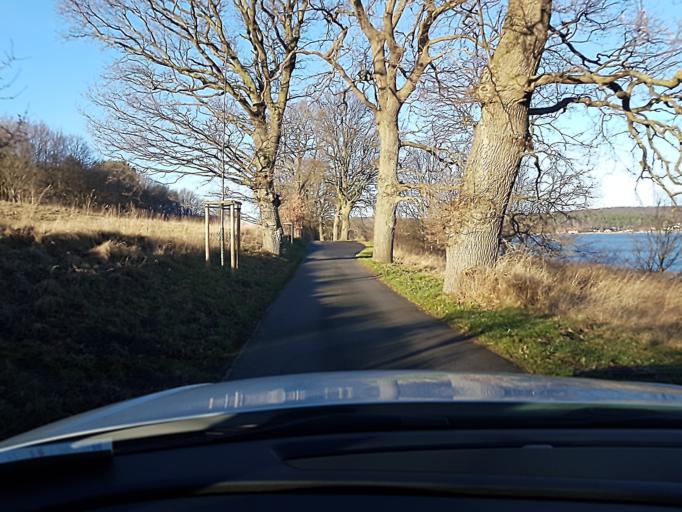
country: DE
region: Mecklenburg-Vorpommern
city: Ostseebad Sellin
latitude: 54.3622
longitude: 13.6834
